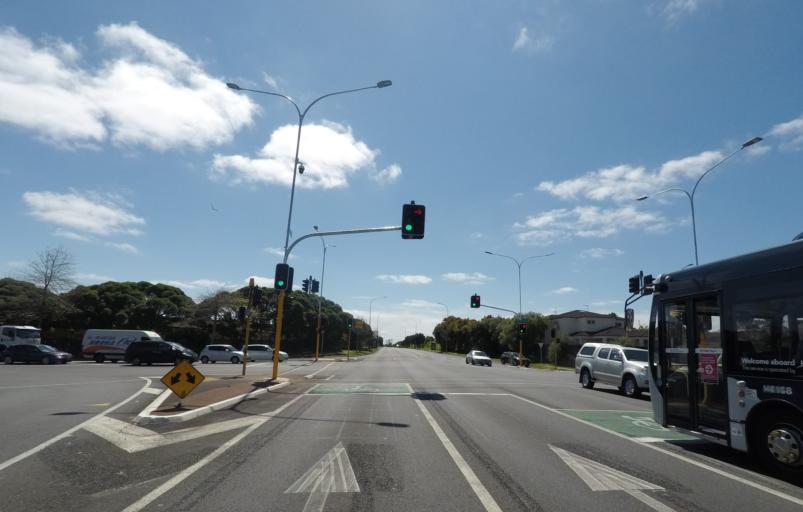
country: NZ
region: Auckland
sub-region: Auckland
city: Manukau City
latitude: -36.9432
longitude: 174.9125
